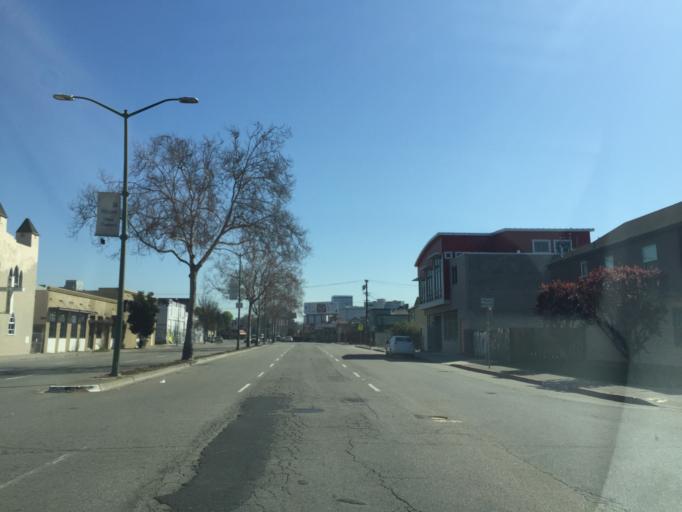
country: US
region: California
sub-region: Alameda County
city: Oakland
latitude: 37.8152
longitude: -122.2819
